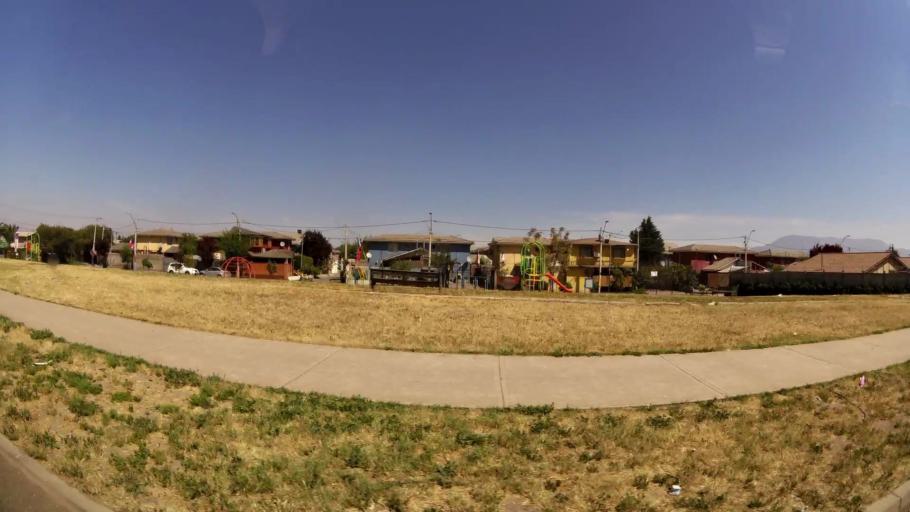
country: CL
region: Santiago Metropolitan
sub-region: Provincia de Santiago
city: Lo Prado
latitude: -33.3957
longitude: -70.7426
